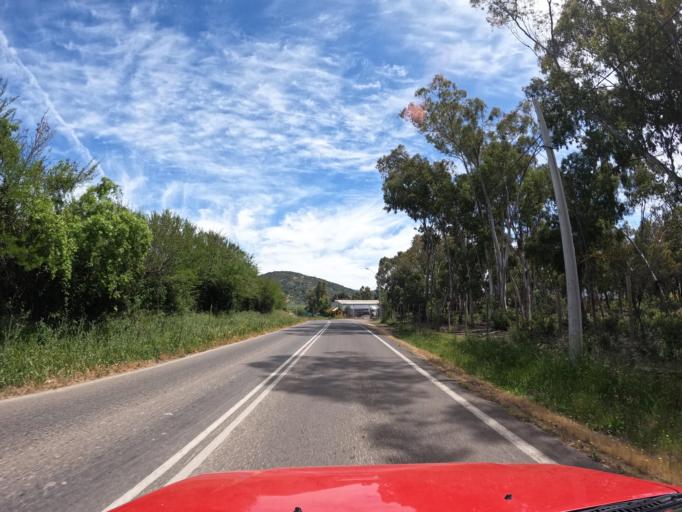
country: CL
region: Maule
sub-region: Provincia de Talca
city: Talca
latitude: -35.1178
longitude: -71.6441
